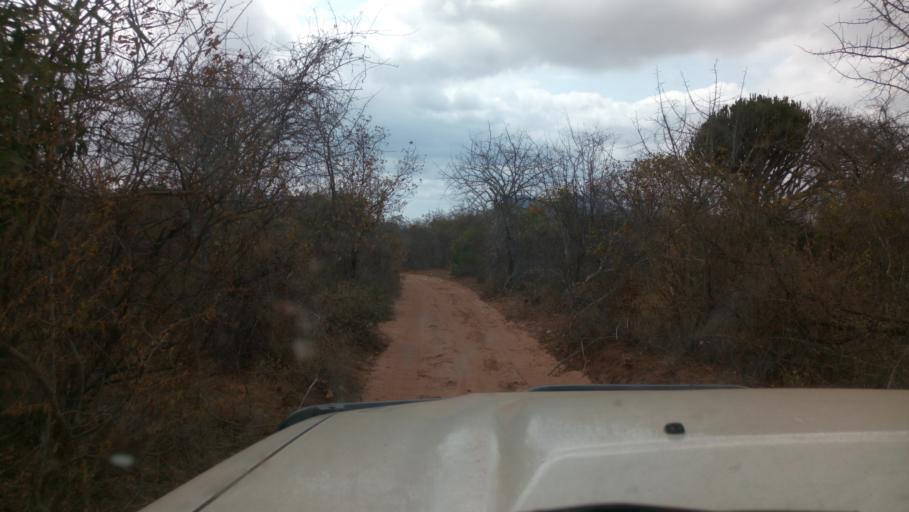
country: KE
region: Kitui
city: Kitui
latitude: -1.8475
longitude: 38.3502
